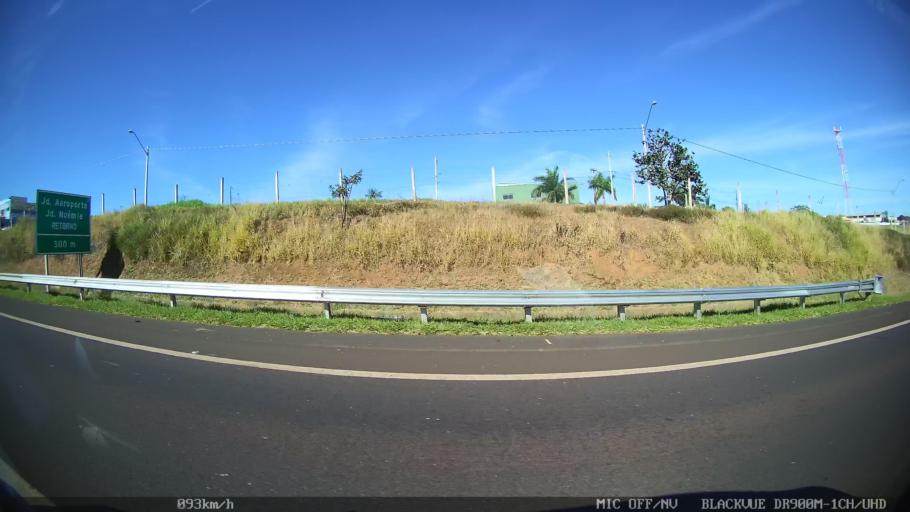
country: BR
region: Sao Paulo
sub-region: Franca
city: Franca
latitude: -20.5724
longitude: -47.3811
